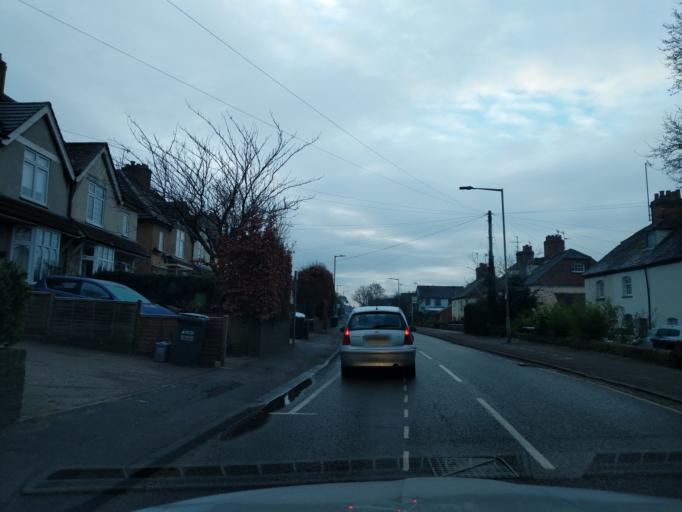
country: GB
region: England
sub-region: Hertfordshire
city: Kings Langley
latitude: 51.7106
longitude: -0.4405
